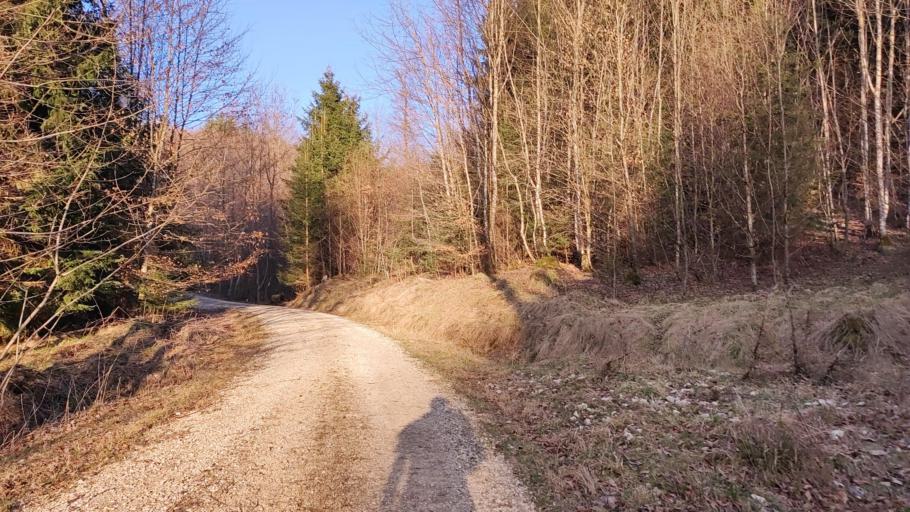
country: DE
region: Bavaria
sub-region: Swabia
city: Zusmarshausen
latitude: 48.4290
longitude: 10.6196
